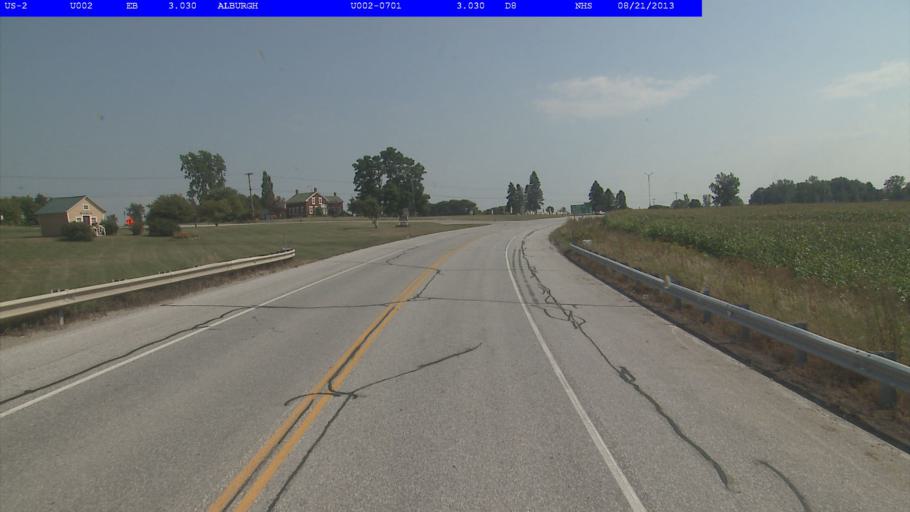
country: US
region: New York
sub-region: Clinton County
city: Rouses Point
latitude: 44.9900
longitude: -73.2972
